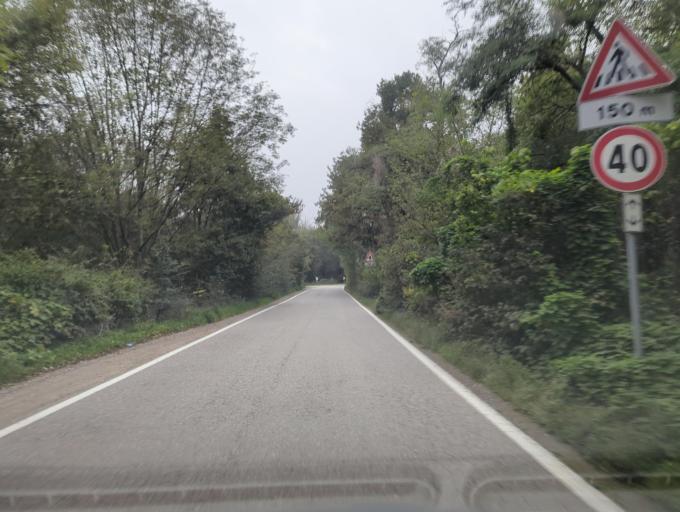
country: IT
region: Lombardy
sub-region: Citta metropolitana di Milano
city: Nosate
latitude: 45.5595
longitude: 8.7392
